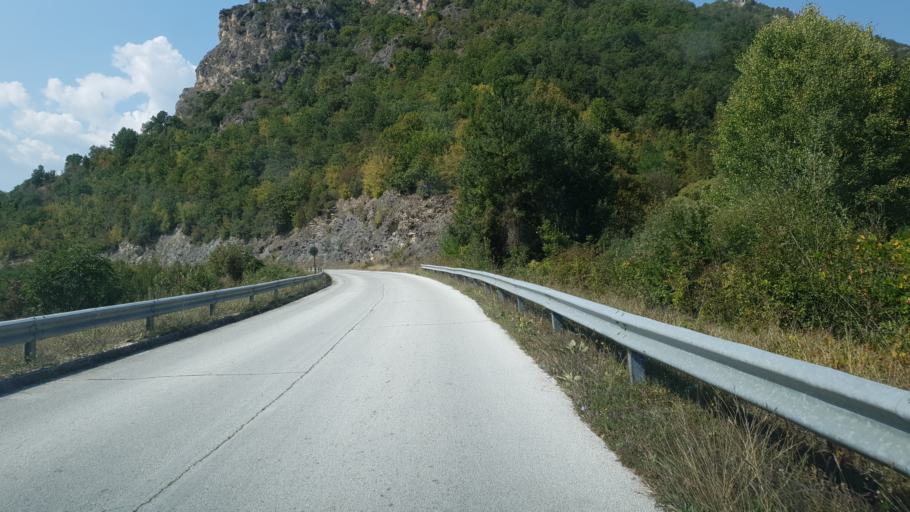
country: MK
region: Makedonski Brod
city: Samokov
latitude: 41.6671
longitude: 21.2331
